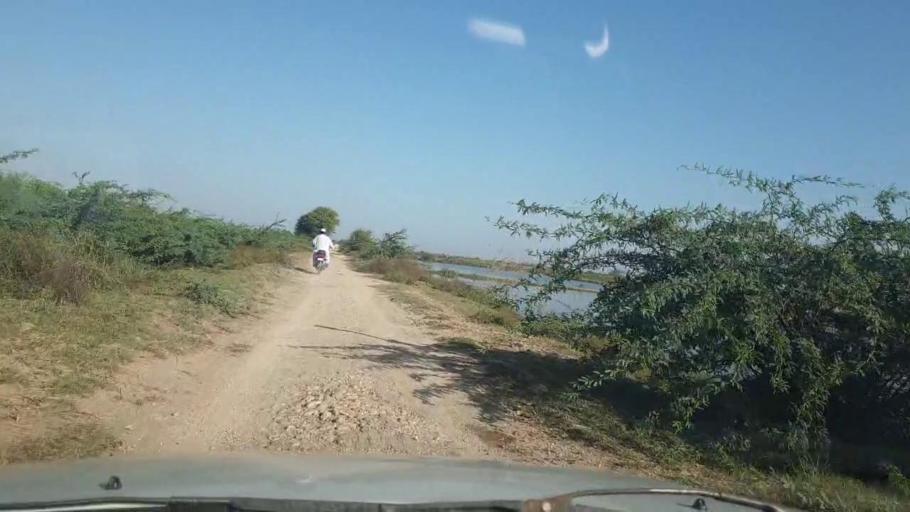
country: PK
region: Sindh
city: Chuhar Jamali
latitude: 24.5469
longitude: 67.9109
